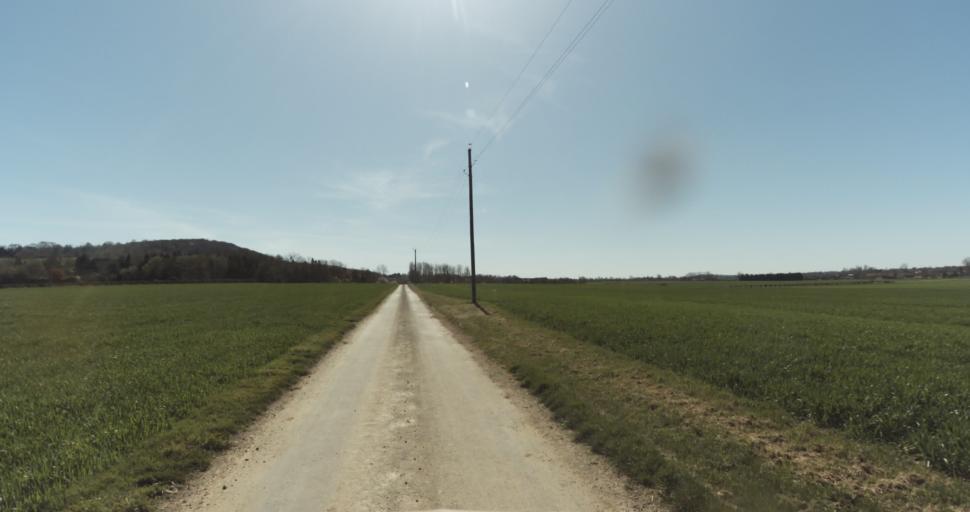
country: FR
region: Lower Normandy
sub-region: Departement du Calvados
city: Saint-Pierre-sur-Dives
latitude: 49.0210
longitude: 0.0317
